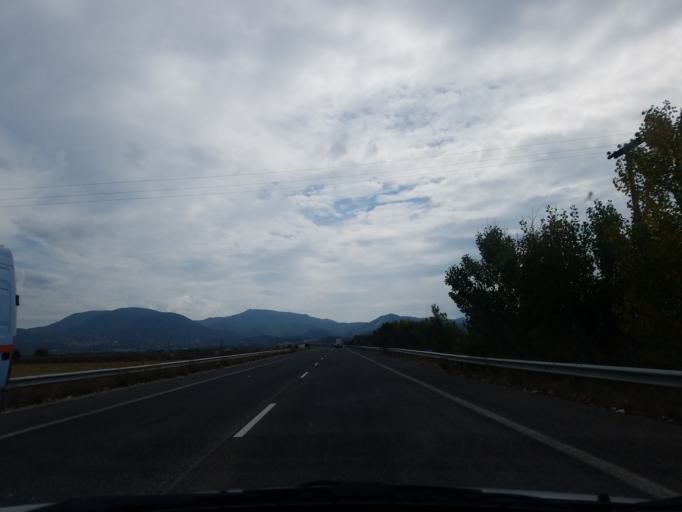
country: GR
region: Central Greece
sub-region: Nomos Fthiotidos
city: Domokos
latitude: 39.0462
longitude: 22.3484
